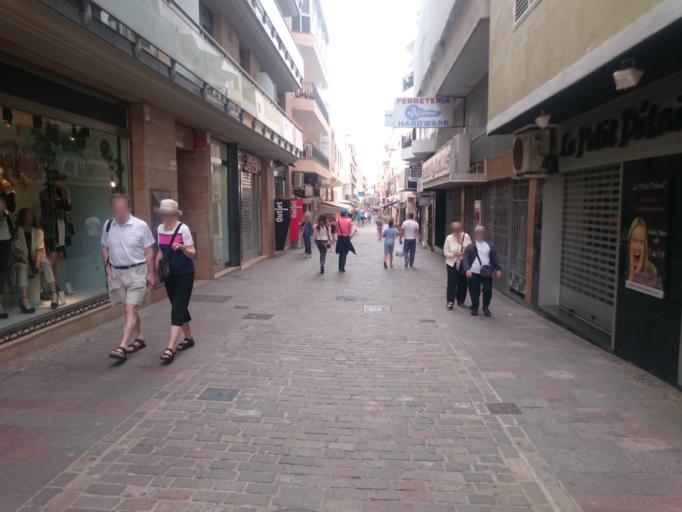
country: ES
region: Canary Islands
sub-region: Provincia de Santa Cruz de Tenerife
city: Playa de las Americas
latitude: 28.0521
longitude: -16.7177
